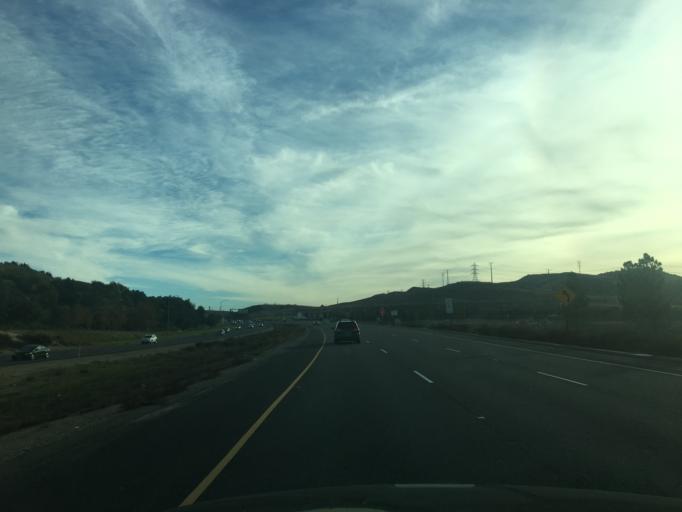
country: US
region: California
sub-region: Orange County
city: Laguna Woods
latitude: 33.6468
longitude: -117.7622
